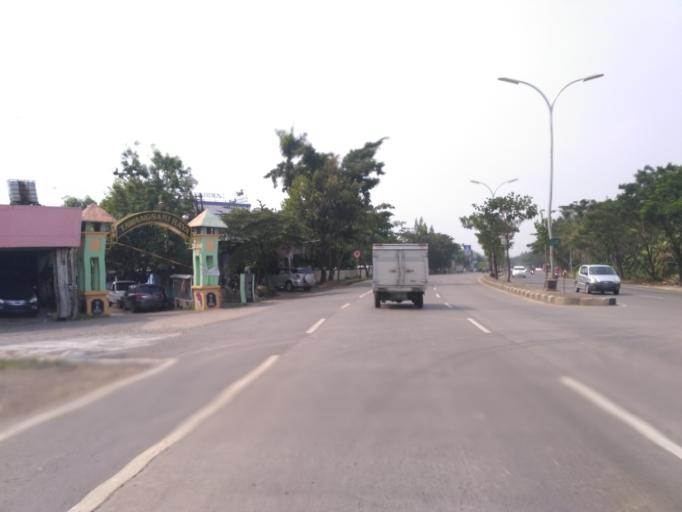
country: ID
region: Central Java
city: Semarang
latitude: -6.9729
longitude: 110.3883
